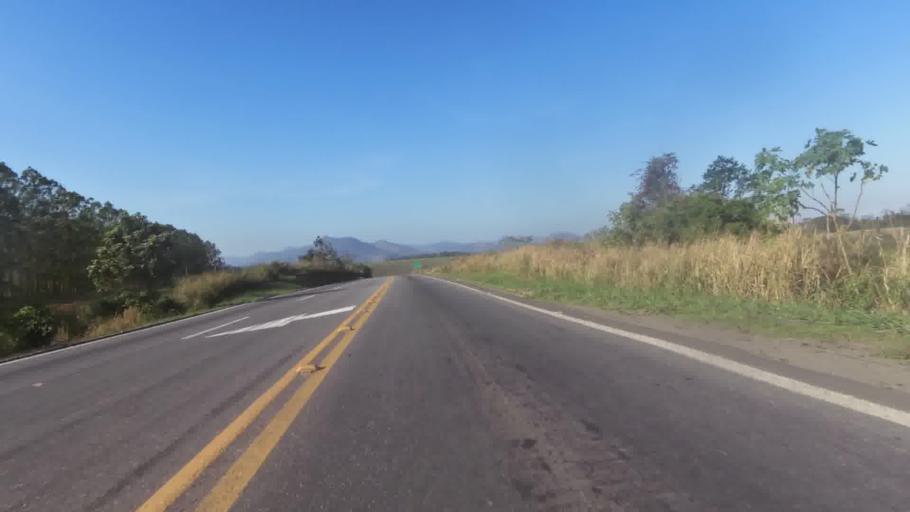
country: BR
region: Espirito Santo
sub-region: Alfredo Chaves
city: Alfredo Chaves
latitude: -20.6951
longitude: -40.7079
